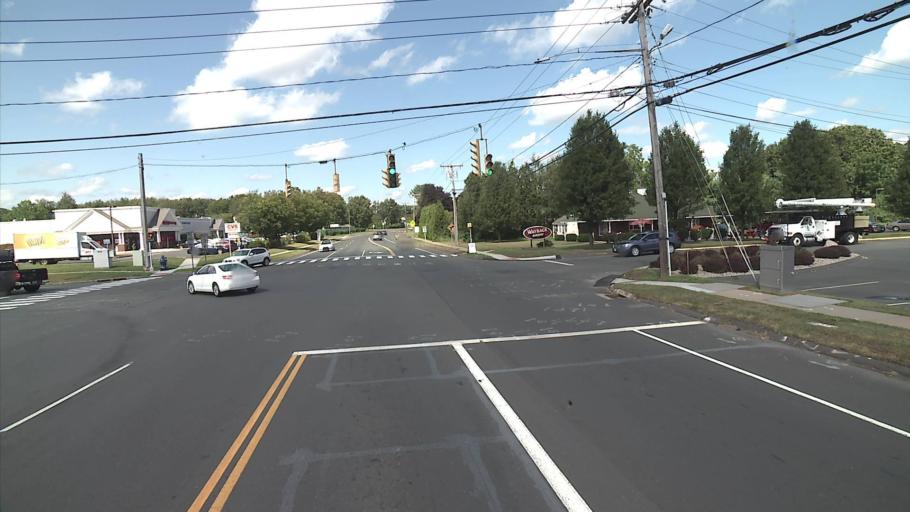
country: US
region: Connecticut
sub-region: Hartford County
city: Newington
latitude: 41.6607
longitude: -72.6786
